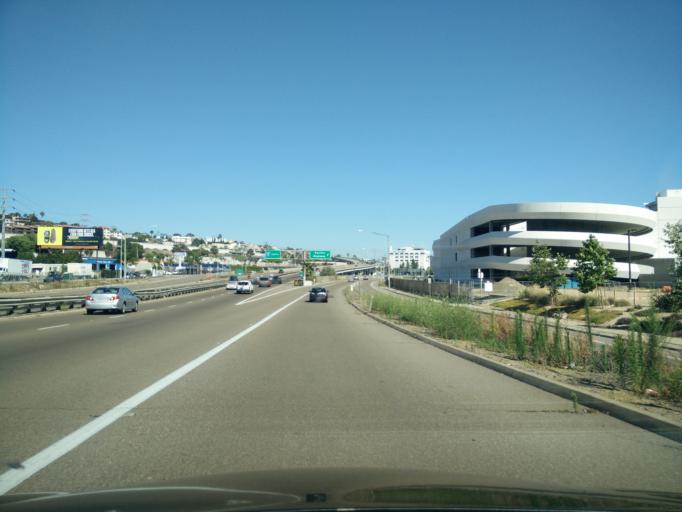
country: US
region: California
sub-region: San Diego County
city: San Diego
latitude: 32.7396
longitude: -117.1826
